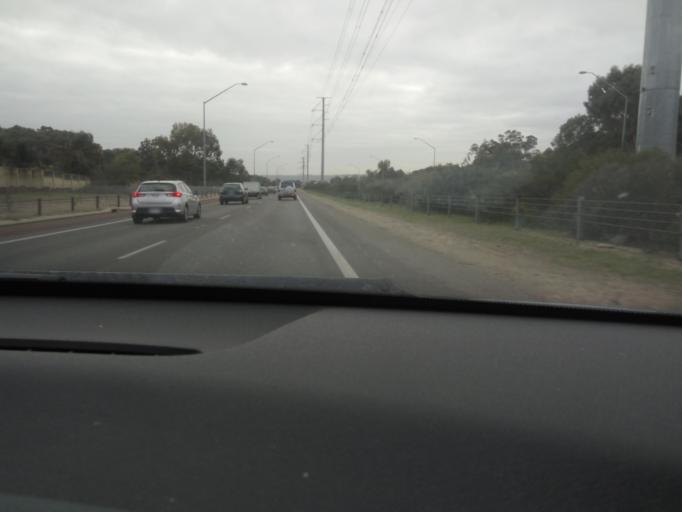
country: AU
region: Western Australia
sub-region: Gosnells
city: Langford
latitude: -32.0420
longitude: 115.9520
